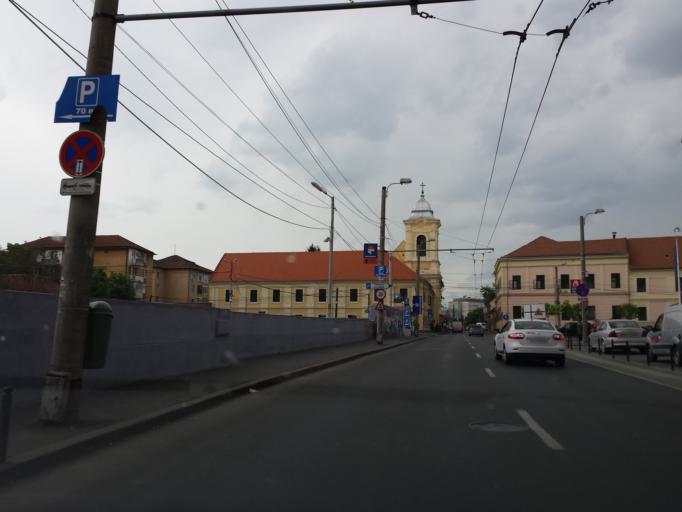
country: RO
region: Timis
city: Timisoara
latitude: 45.7546
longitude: 21.2250
